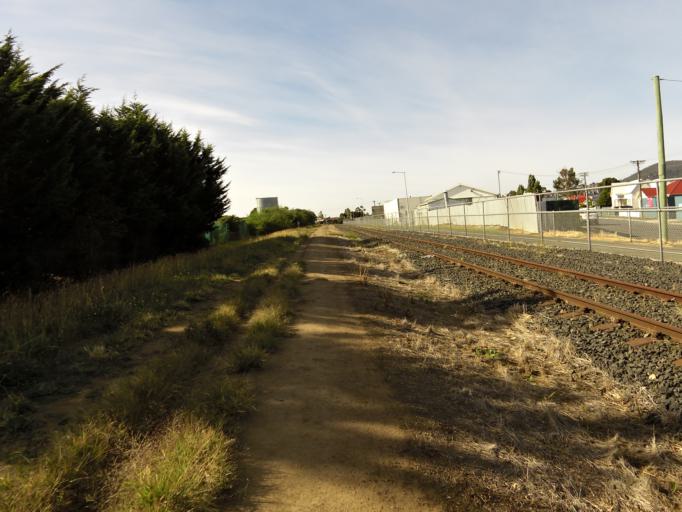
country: AU
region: Tasmania
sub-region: Glenorchy
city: Moonah
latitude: -42.8436
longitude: 147.2958
